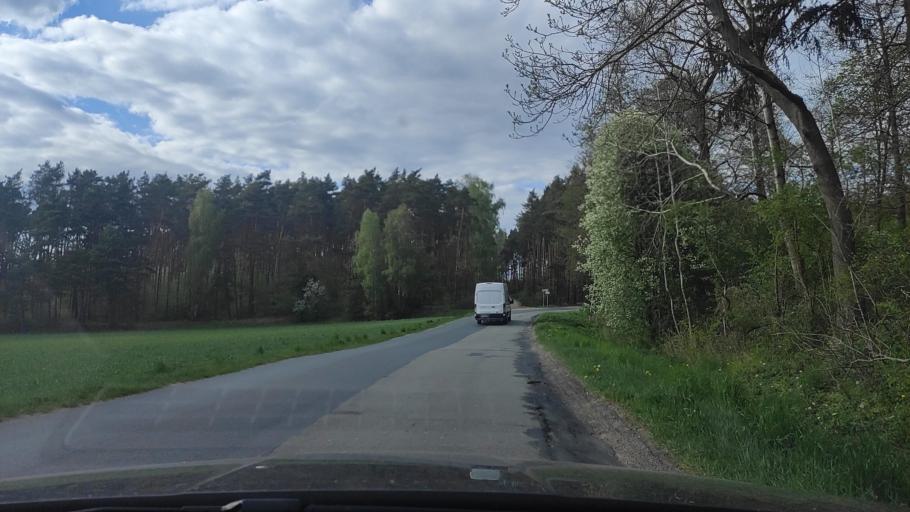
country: PL
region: Greater Poland Voivodeship
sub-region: Powiat poznanski
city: Kobylnica
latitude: 52.4503
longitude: 17.1609
